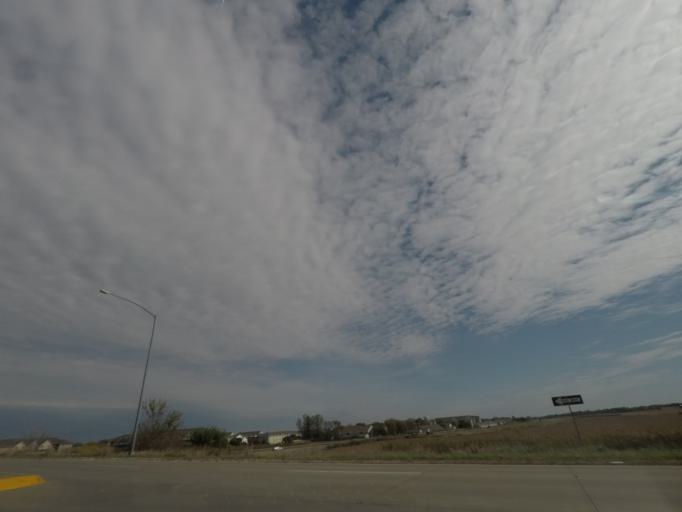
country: US
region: Iowa
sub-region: Story County
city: Ames
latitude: 42.0070
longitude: -93.6787
